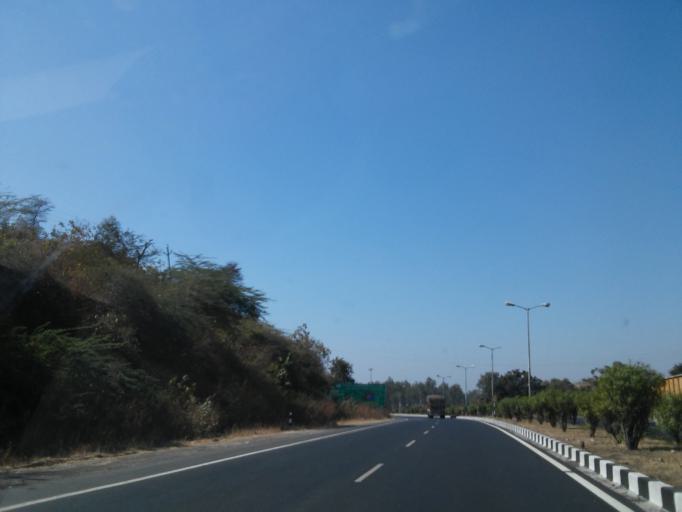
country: IN
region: Gujarat
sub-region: Sabar Kantha
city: Modasa
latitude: 23.6171
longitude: 73.2590
